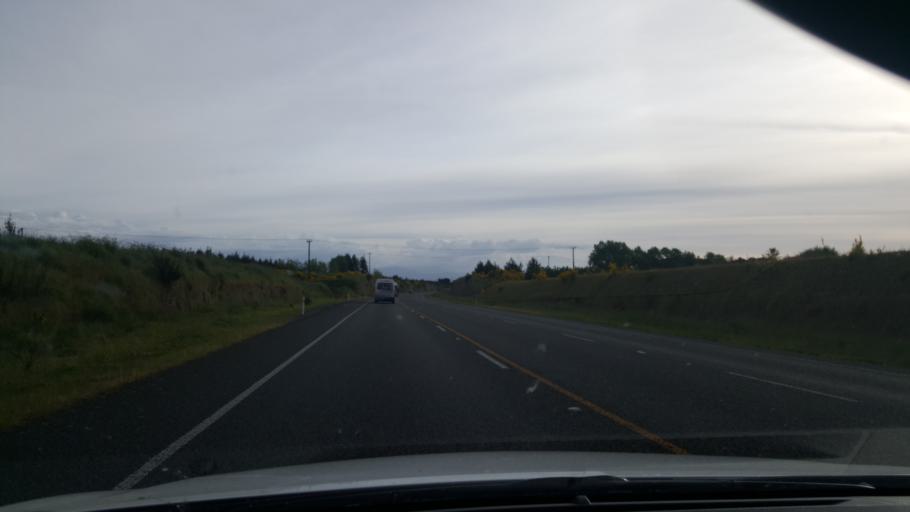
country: NZ
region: Waikato
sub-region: Taupo District
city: Taupo
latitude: -38.7190
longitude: 176.1028
